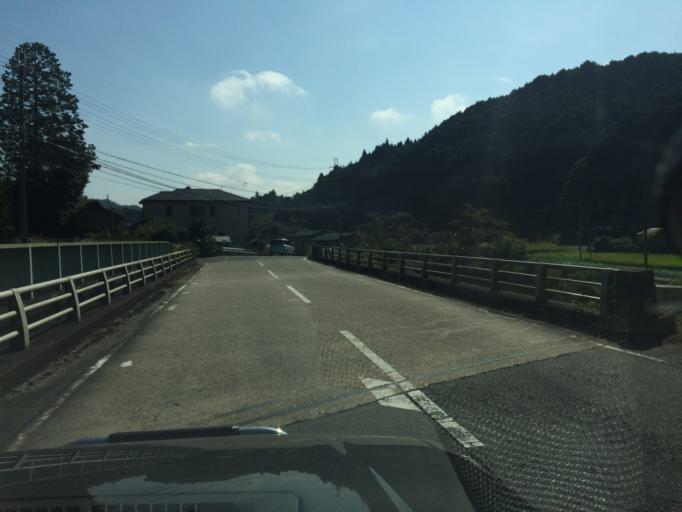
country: JP
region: Nara
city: Nara-shi
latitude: 34.7355
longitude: 135.9641
